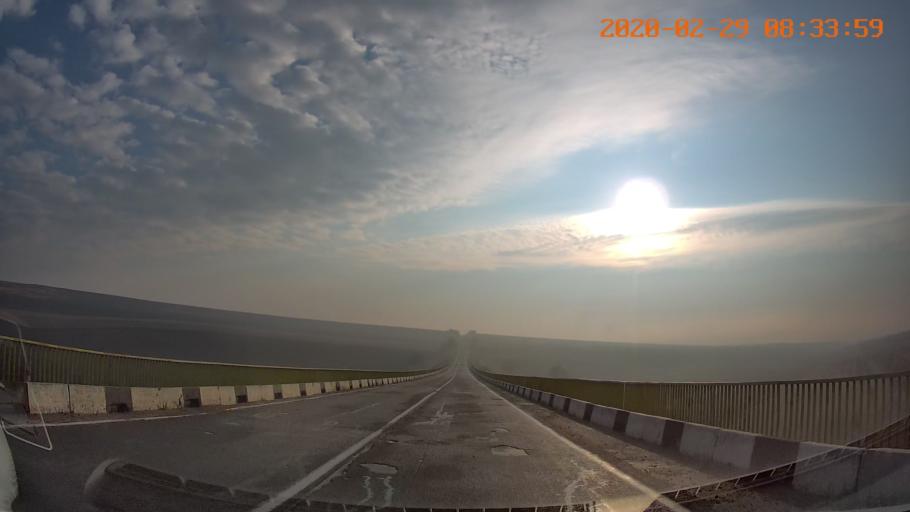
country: MD
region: Anenii Noi
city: Anenii Noi
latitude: 46.9261
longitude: 29.3008
